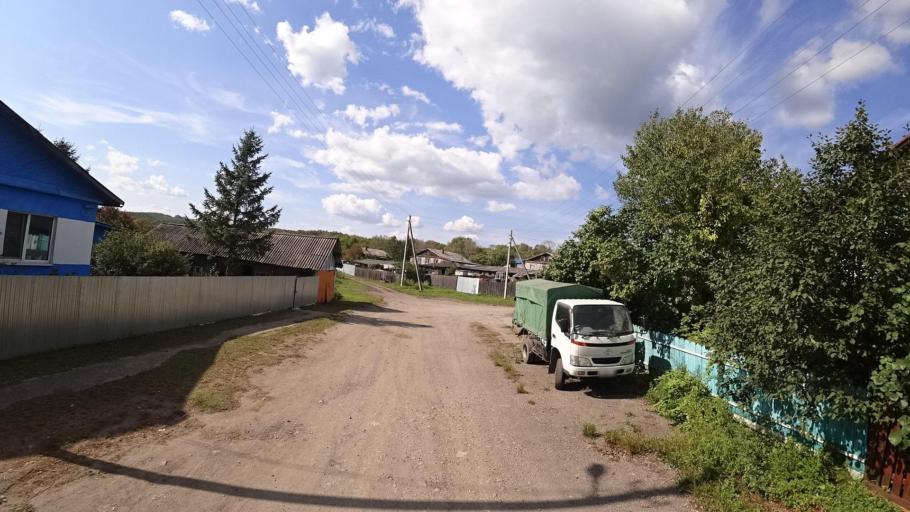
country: RU
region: Jewish Autonomous Oblast
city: Birakan
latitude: 49.0098
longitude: 131.7418
